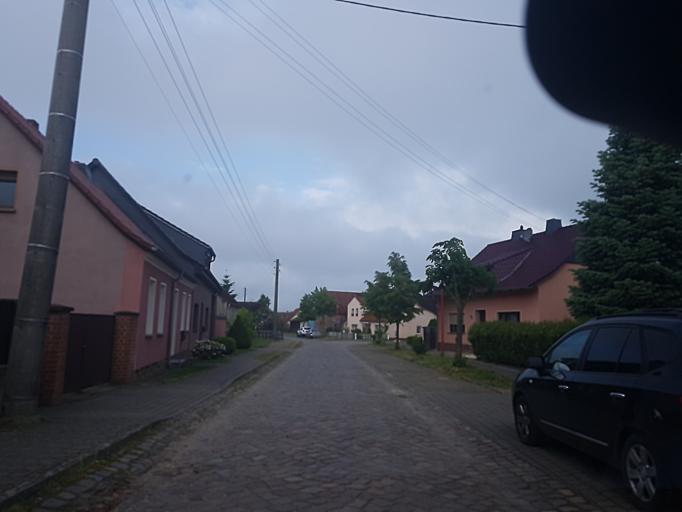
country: DE
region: Saxony-Anhalt
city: Klieken
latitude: 52.0080
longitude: 12.3726
